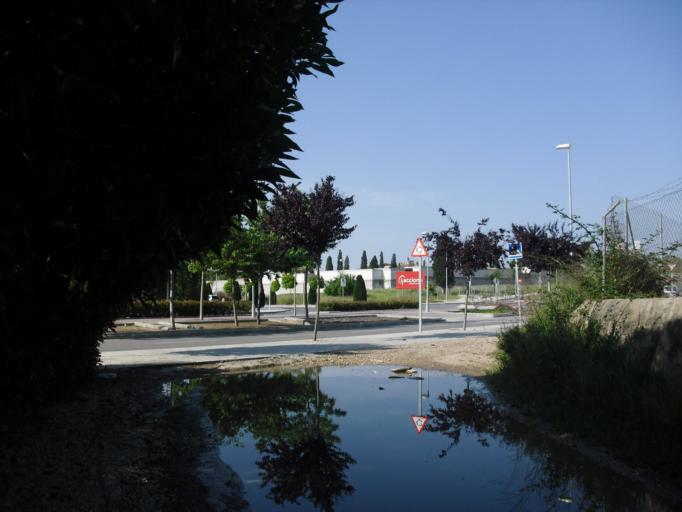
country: ES
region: Catalonia
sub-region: Provincia de Barcelona
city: Vilanova i la Geltru
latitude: 41.2345
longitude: 1.7302
